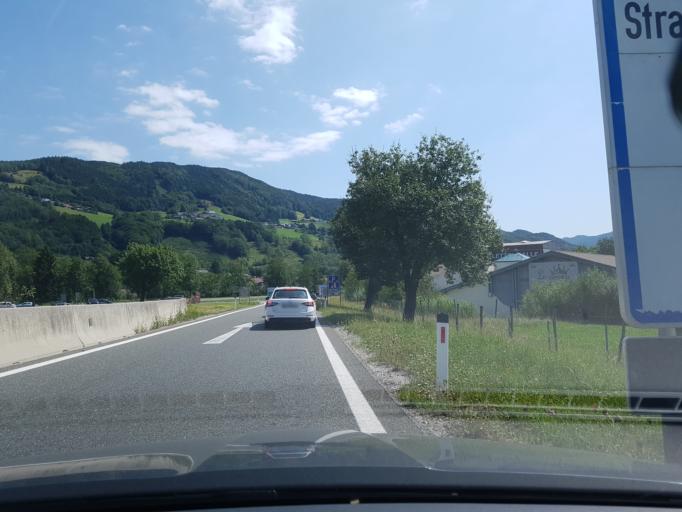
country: AT
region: Upper Austria
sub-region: Politischer Bezirk Vocklabruck
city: Mondsee
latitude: 47.8607
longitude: 13.3373
